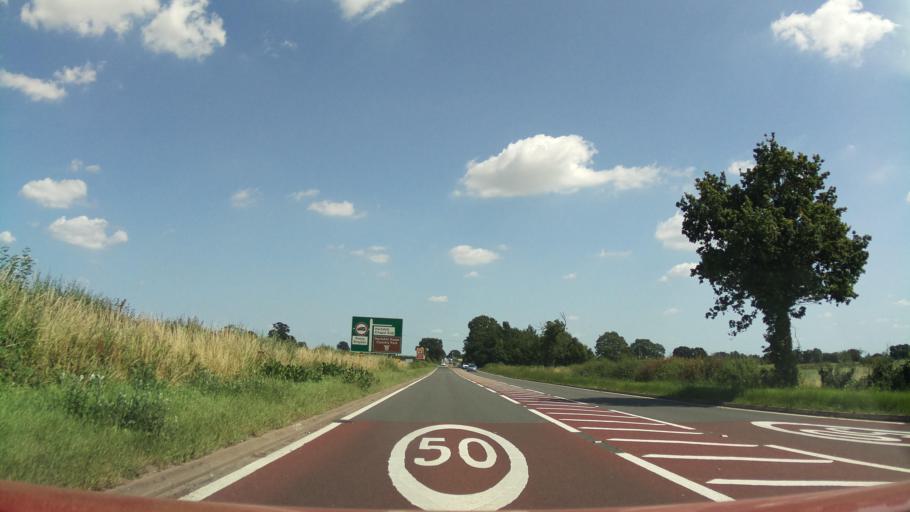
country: GB
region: England
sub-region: Warwickshire
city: Hartshill
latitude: 52.5664
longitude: -1.5094
